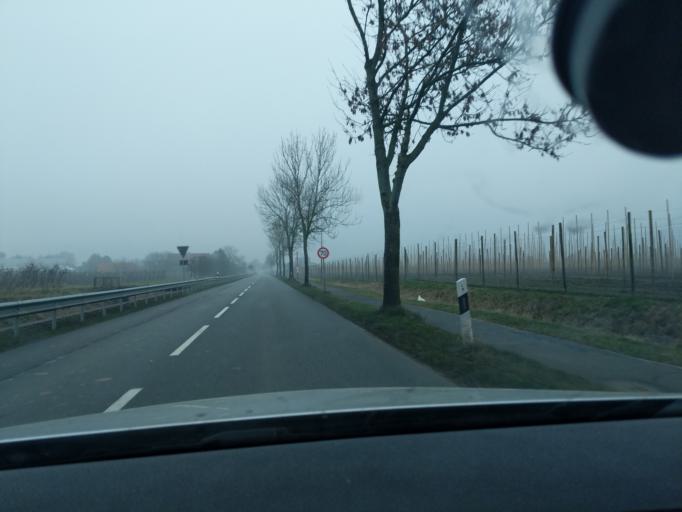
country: DE
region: Lower Saxony
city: Jork
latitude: 53.5395
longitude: 9.6562
